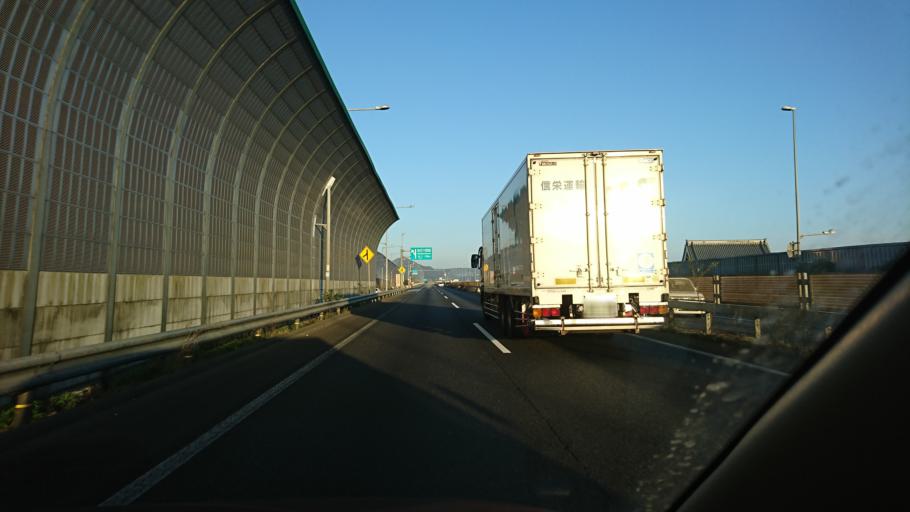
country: JP
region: Hyogo
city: Kakogawacho-honmachi
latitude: 34.7733
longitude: 134.8417
